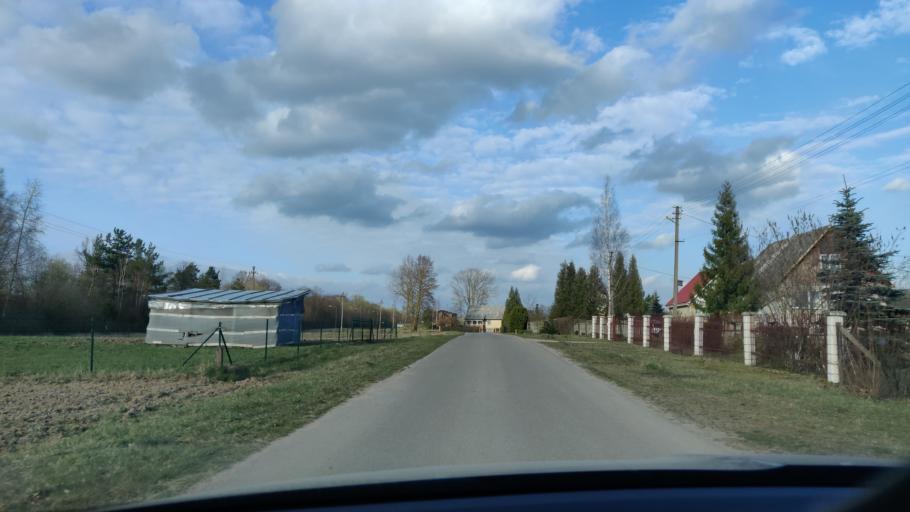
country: LT
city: Trakai
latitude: 54.6083
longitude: 24.9723
